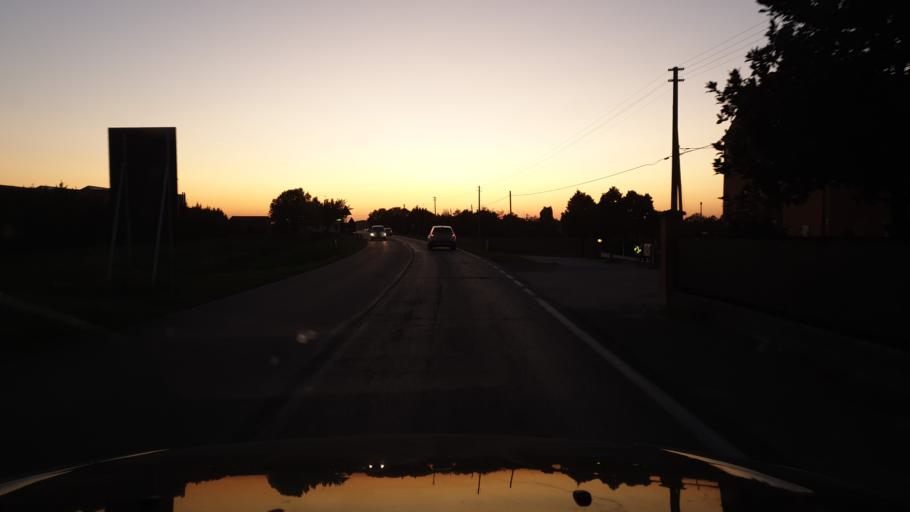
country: IT
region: Emilia-Romagna
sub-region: Provincia di Bologna
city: Altedo
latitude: 44.6840
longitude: 11.4889
